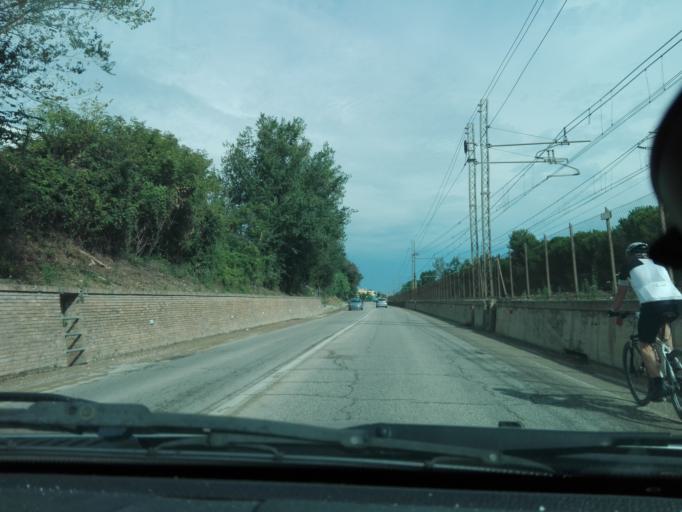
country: IT
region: Abruzzo
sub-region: Provincia di Teramo
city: Pineto
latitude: 42.5909
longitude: 14.0830
